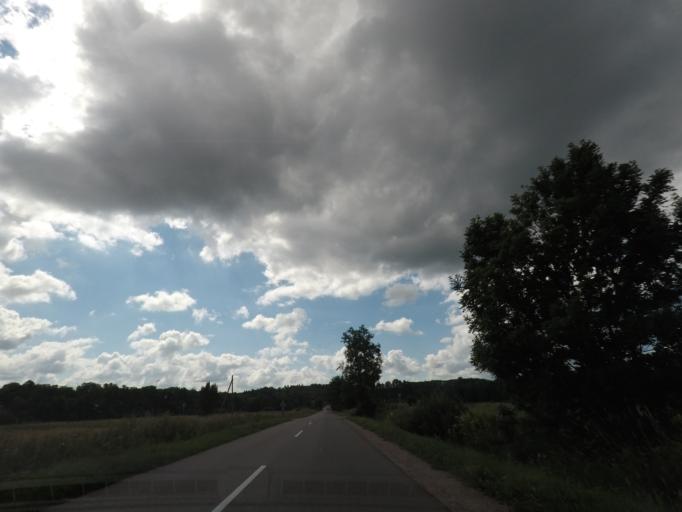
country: PL
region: Pomeranian Voivodeship
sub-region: Powiat wejherowski
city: Leczyce
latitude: 54.5808
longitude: 17.8652
